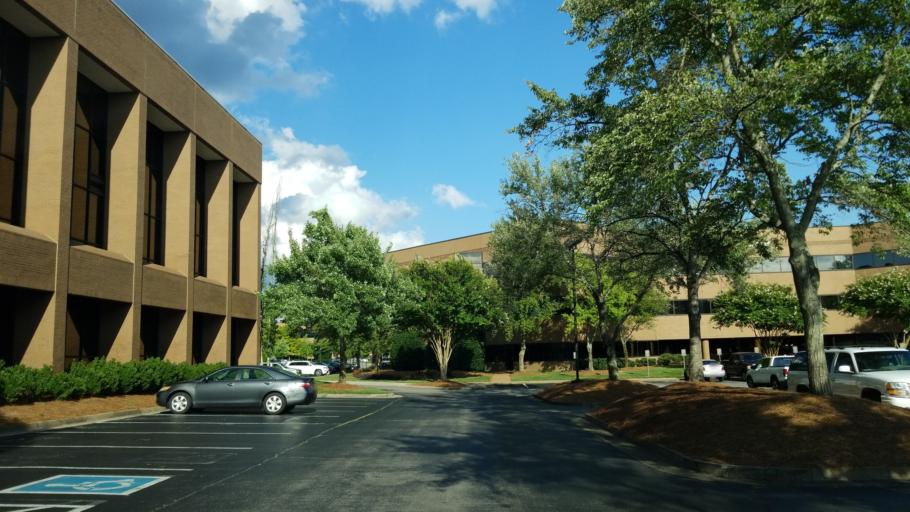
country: US
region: Tennessee
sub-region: Williamson County
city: Brentwood
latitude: 36.0291
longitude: -86.7902
